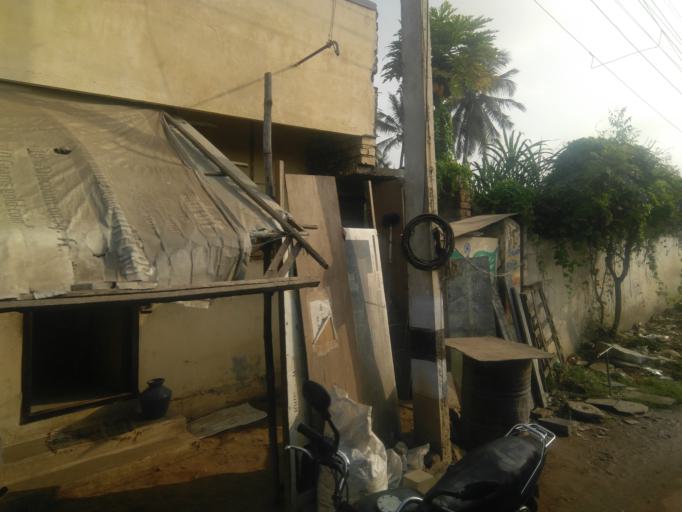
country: IN
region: Tamil Nadu
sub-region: Coimbatore
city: Coimbatore
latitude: 11.0651
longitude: 76.9131
